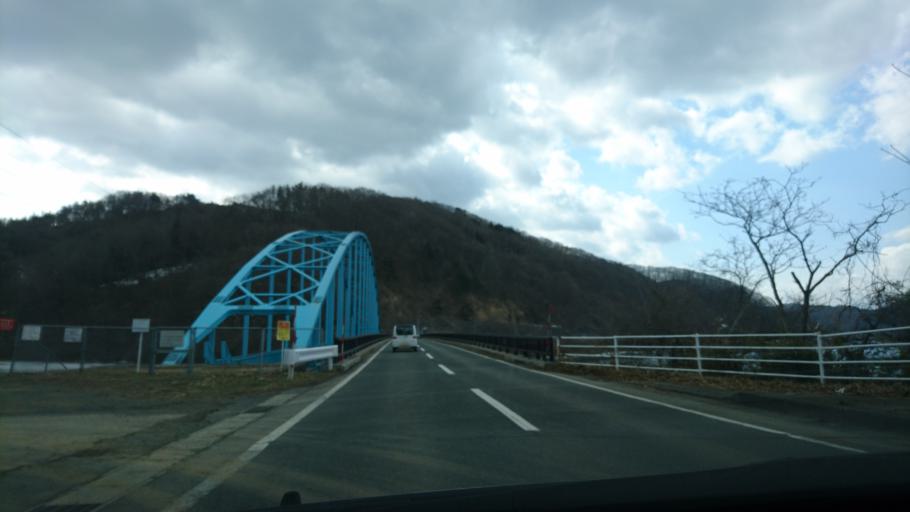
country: JP
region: Iwate
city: Shizukuishi
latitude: 39.6887
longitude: 141.0331
